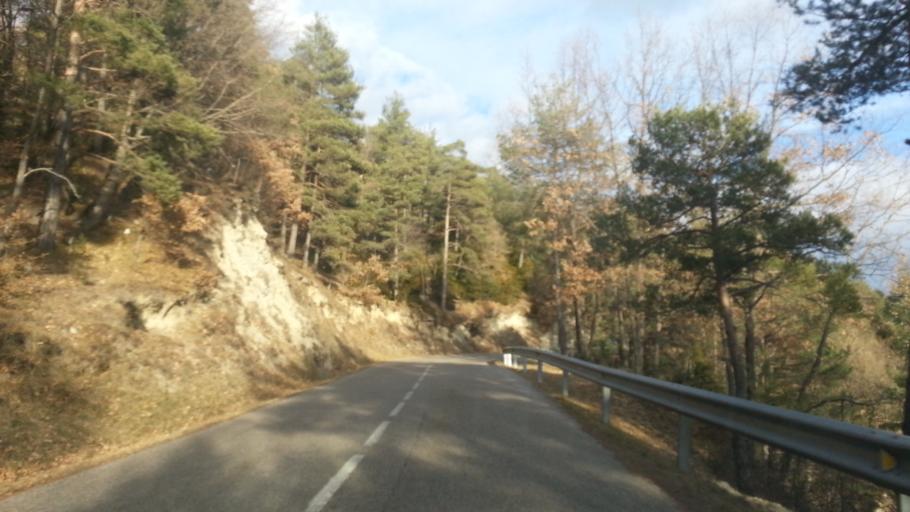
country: ES
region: Catalonia
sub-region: Provincia de Girona
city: Toses
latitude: 42.2466
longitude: 2.0341
